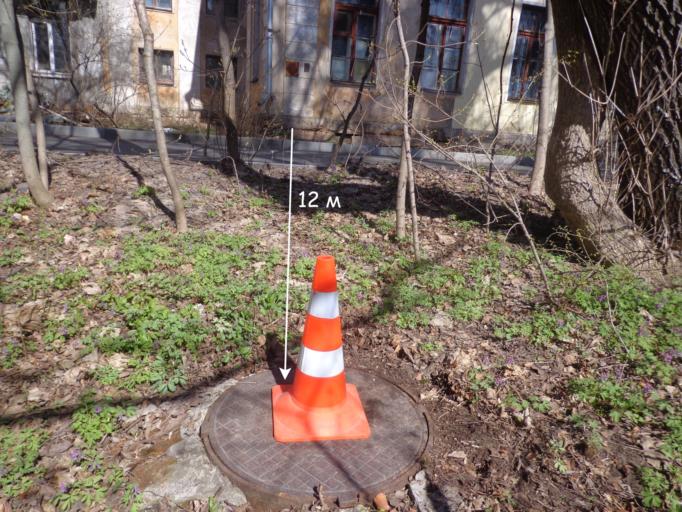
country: RU
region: Voronezj
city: Voronezh
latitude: 51.7090
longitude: 39.2266
